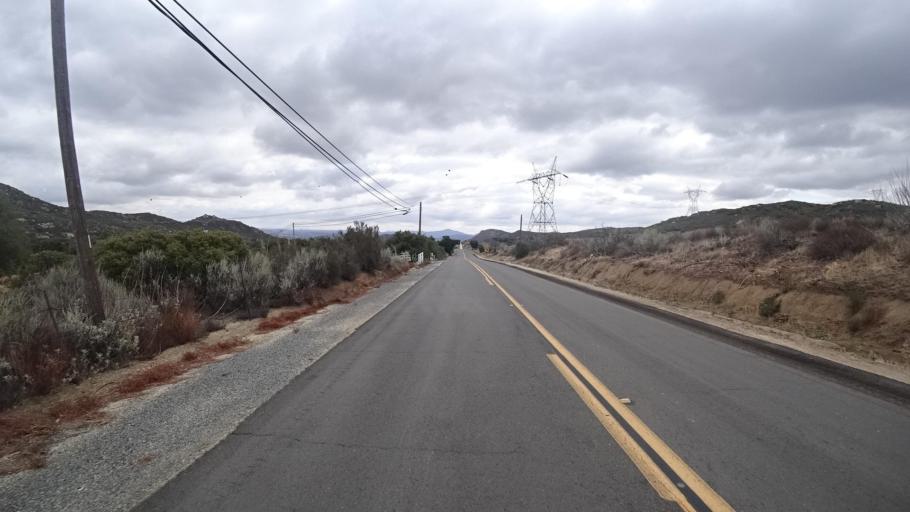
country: US
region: California
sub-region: San Diego County
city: Campo
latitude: 32.6641
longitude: -116.5018
